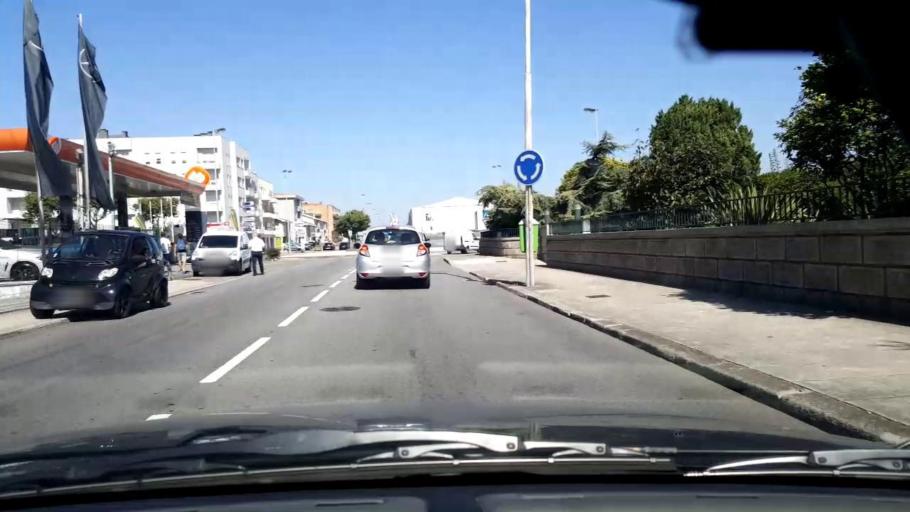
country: PT
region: Porto
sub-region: Vila do Conde
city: Vila do Conde
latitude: 41.3598
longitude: -8.7442
